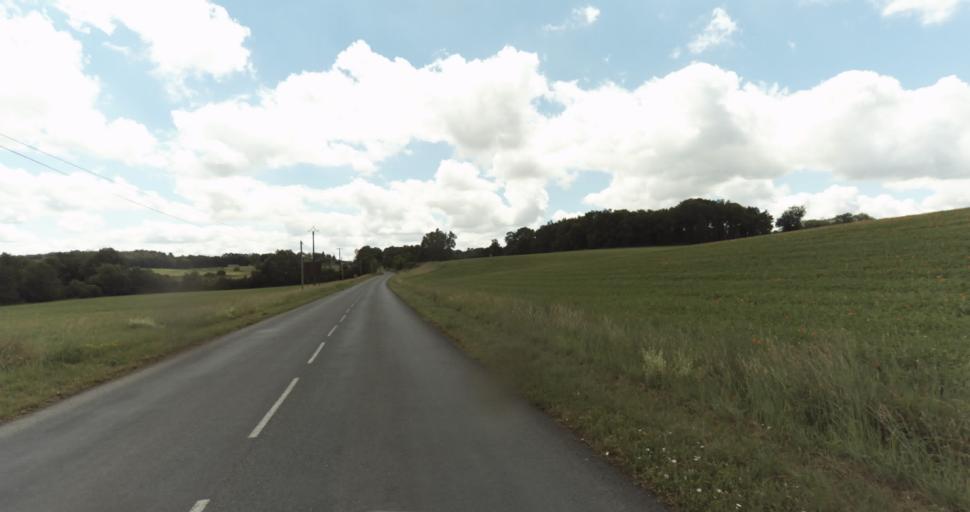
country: FR
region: Aquitaine
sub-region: Departement de la Dordogne
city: Beaumont-du-Perigord
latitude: 44.7380
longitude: 0.7518
